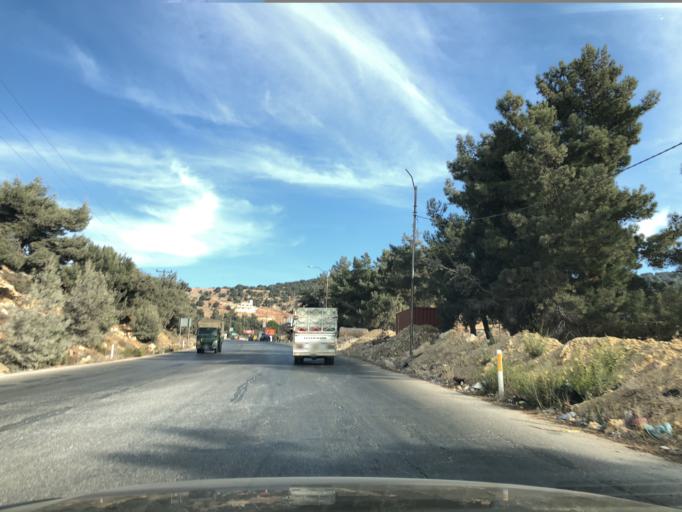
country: JO
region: Irbid
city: `Anjarah
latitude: 32.3135
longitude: 35.7745
